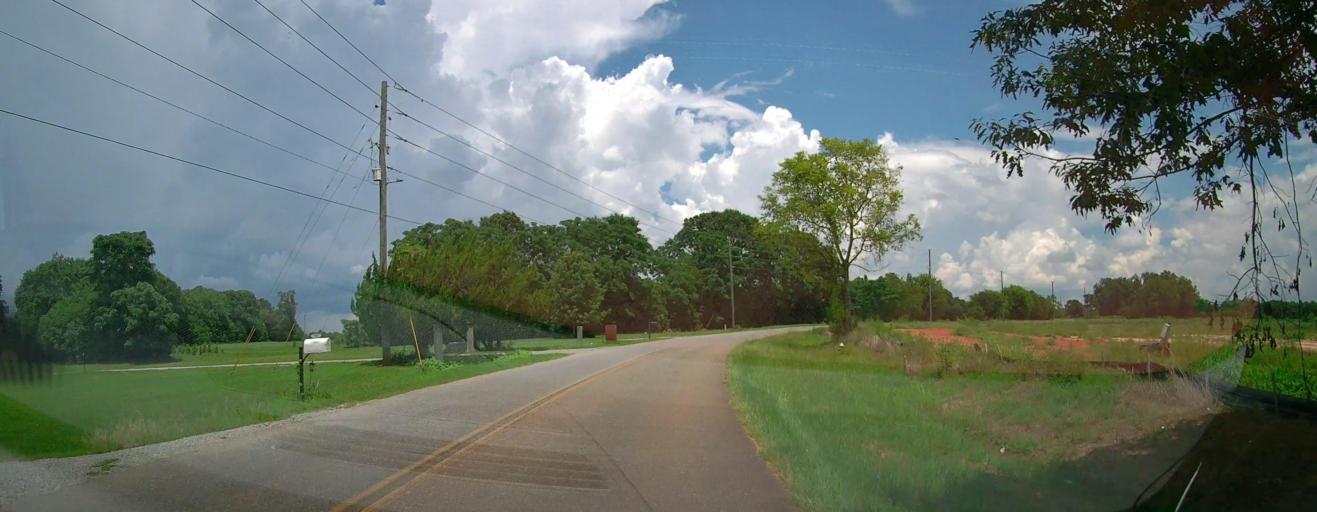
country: US
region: Georgia
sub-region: Houston County
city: Perry
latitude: 32.4967
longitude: -83.6422
